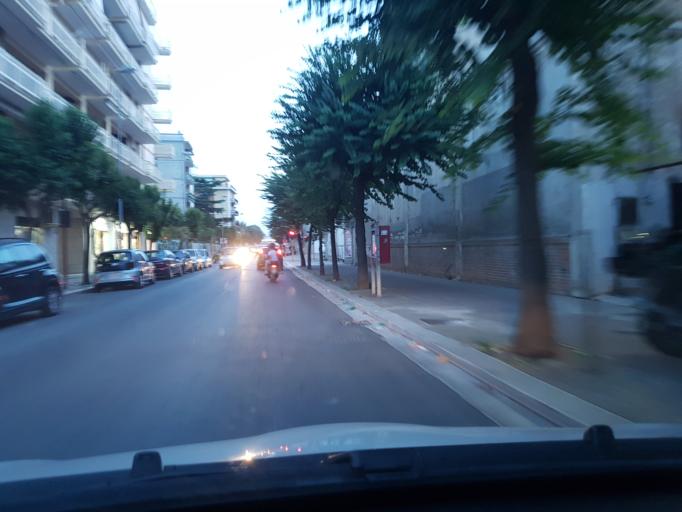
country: IT
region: Apulia
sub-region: Provincia di Foggia
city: Cerignola
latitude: 41.2623
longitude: 15.9080
